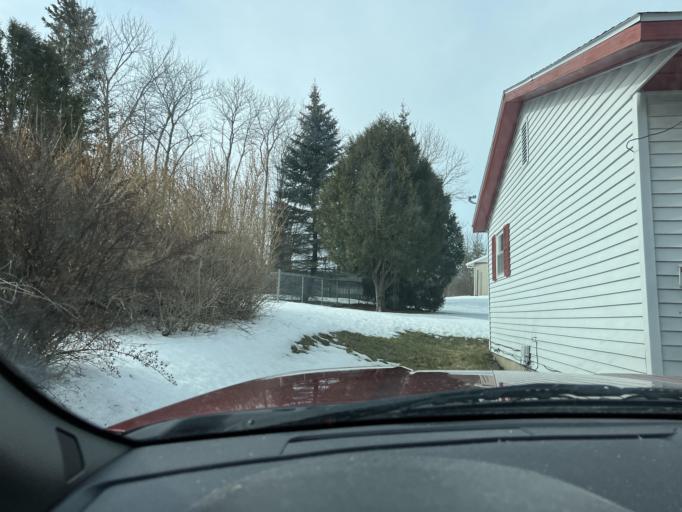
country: US
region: Michigan
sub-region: Mackinac County
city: Saint Ignace
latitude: 45.8706
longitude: -84.7349
